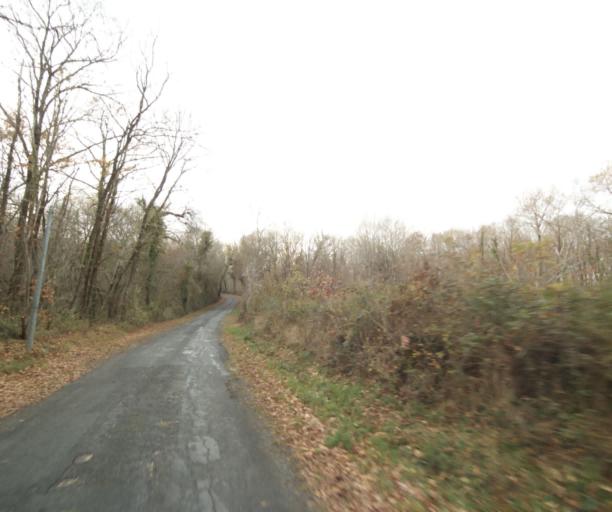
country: FR
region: Poitou-Charentes
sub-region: Departement de la Charente-Maritime
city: Fontcouverte
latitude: 45.7884
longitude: -0.5888
